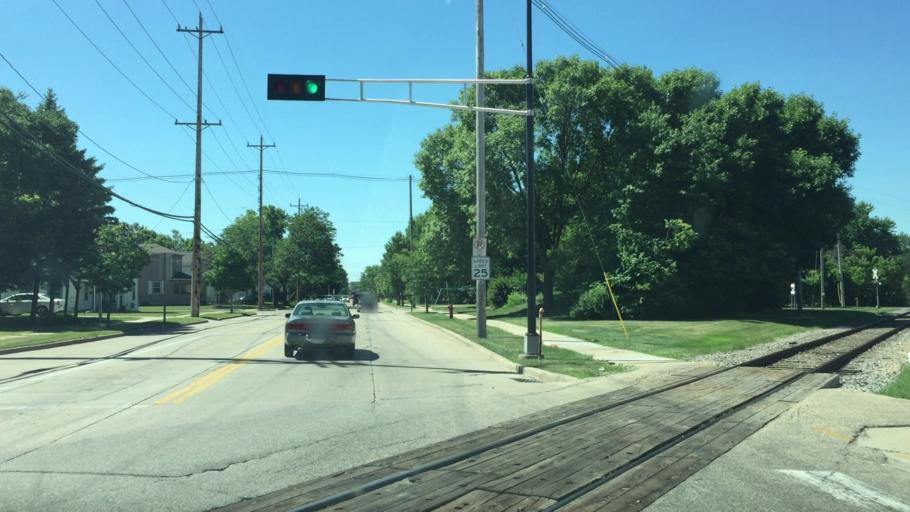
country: US
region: Wisconsin
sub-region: Winnebago County
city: Menasha
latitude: 44.2047
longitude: -88.4532
